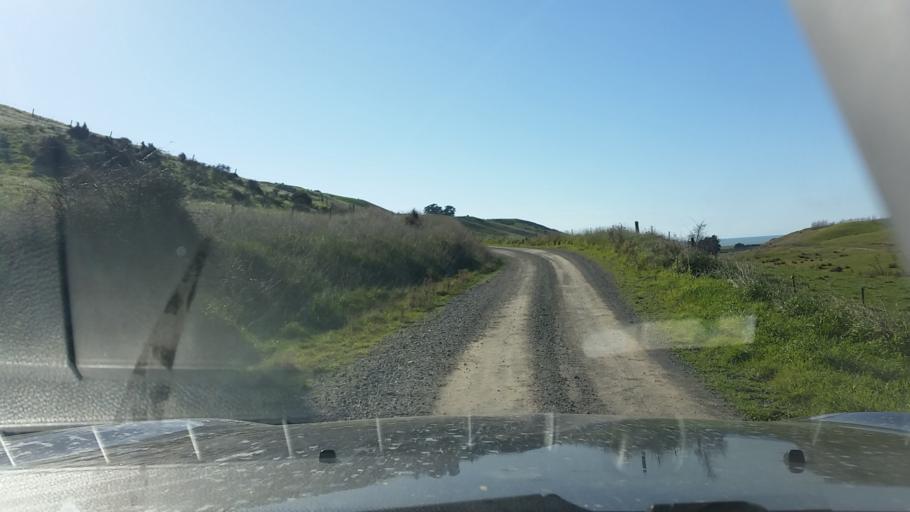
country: NZ
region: Marlborough
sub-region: Marlborough District
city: Blenheim
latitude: -41.6700
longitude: 174.1300
